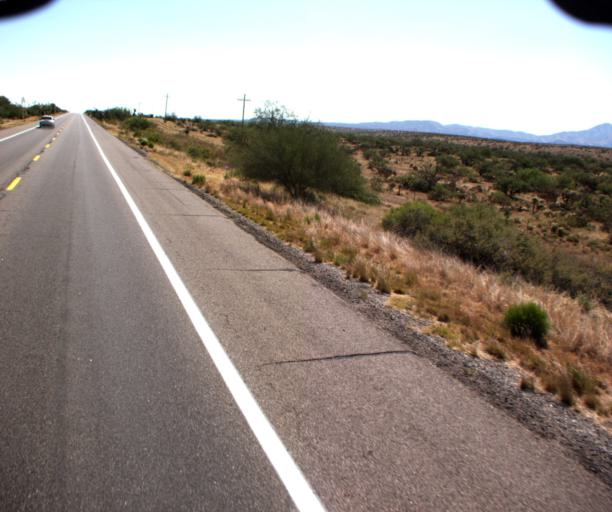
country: US
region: Arizona
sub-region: Pima County
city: Catalina
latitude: 32.5871
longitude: -110.9009
